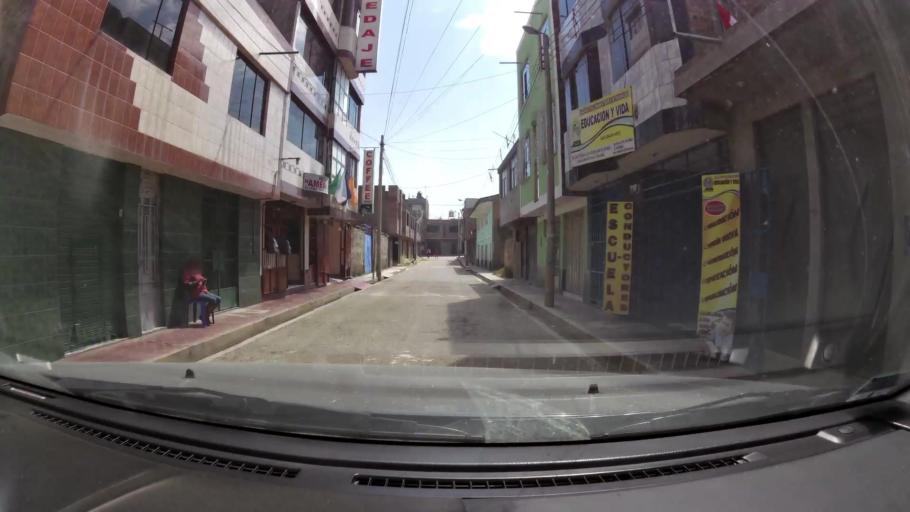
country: PE
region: Junin
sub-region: Provincia de Huancayo
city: Huancayo
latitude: -12.0841
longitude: -75.2057
